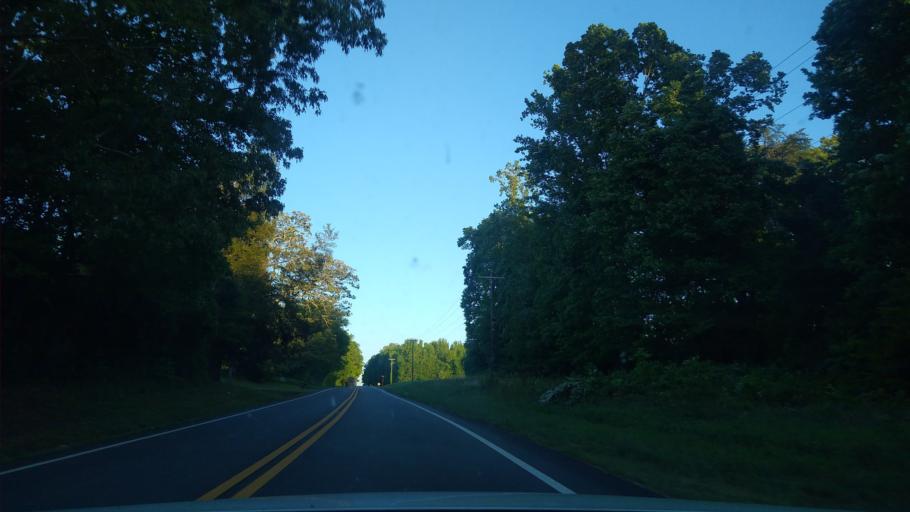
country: US
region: North Carolina
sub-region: Rockingham County
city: Reidsville
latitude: 36.3929
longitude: -79.5126
